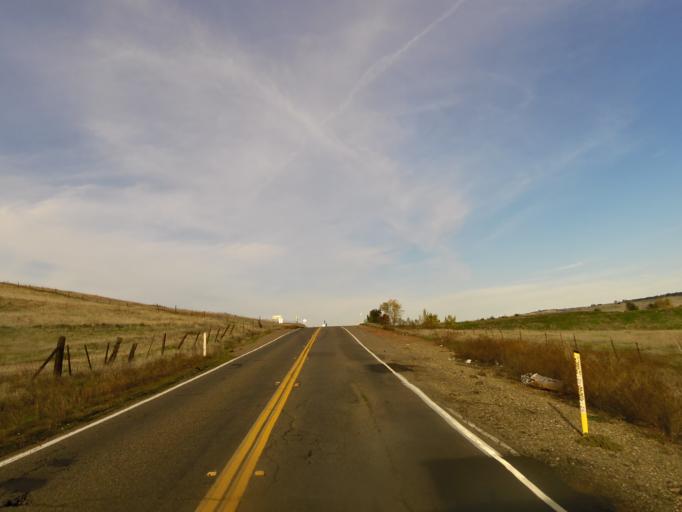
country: US
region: California
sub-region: El Dorado County
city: El Dorado Hills
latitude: 38.6312
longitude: -121.0803
